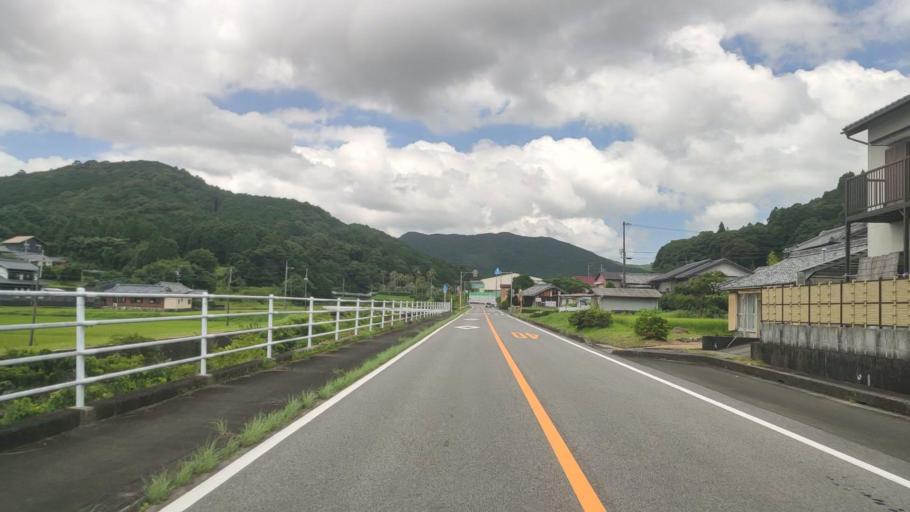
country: JP
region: Mie
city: Toba
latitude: 34.3854
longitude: 136.7990
